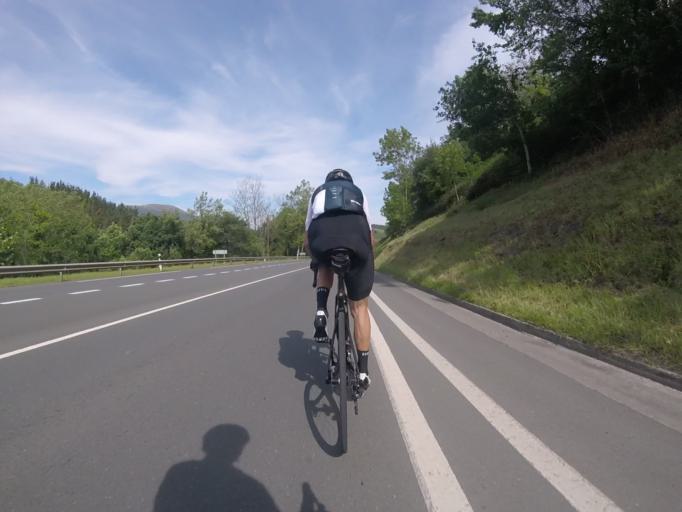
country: ES
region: Basque Country
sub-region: Provincia de Guipuzcoa
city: Cestona
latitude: 43.2585
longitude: -2.2705
